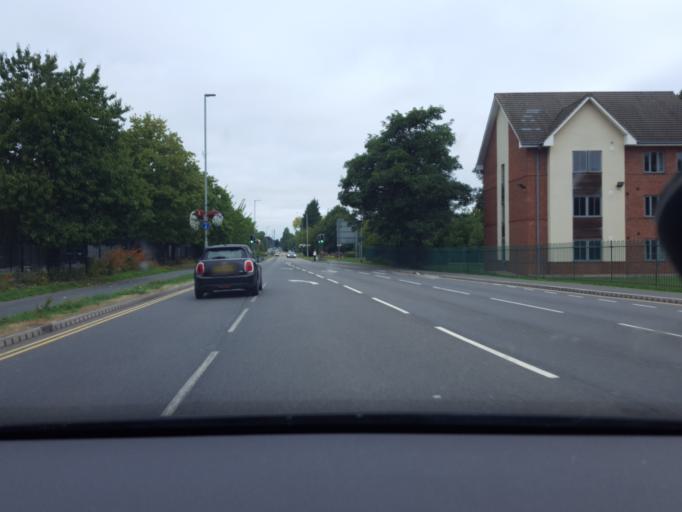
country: GB
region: England
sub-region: Leicestershire
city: Loughborough
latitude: 52.7647
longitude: -1.2188
